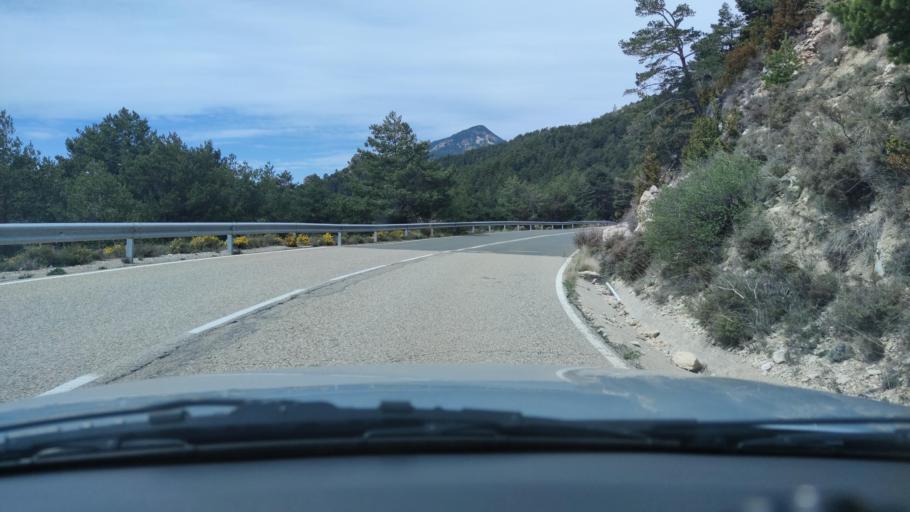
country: ES
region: Catalonia
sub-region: Provincia de Lleida
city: Olius
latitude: 42.1407
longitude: 1.5463
